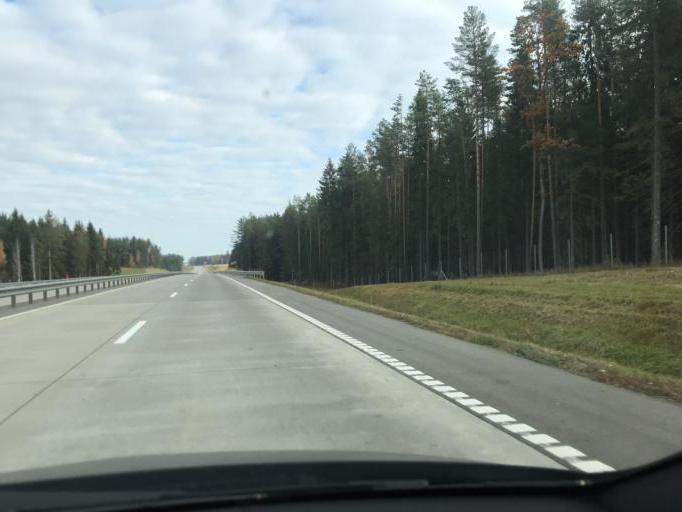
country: BY
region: Minsk
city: Rakaw
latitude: 53.9968
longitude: 27.1180
